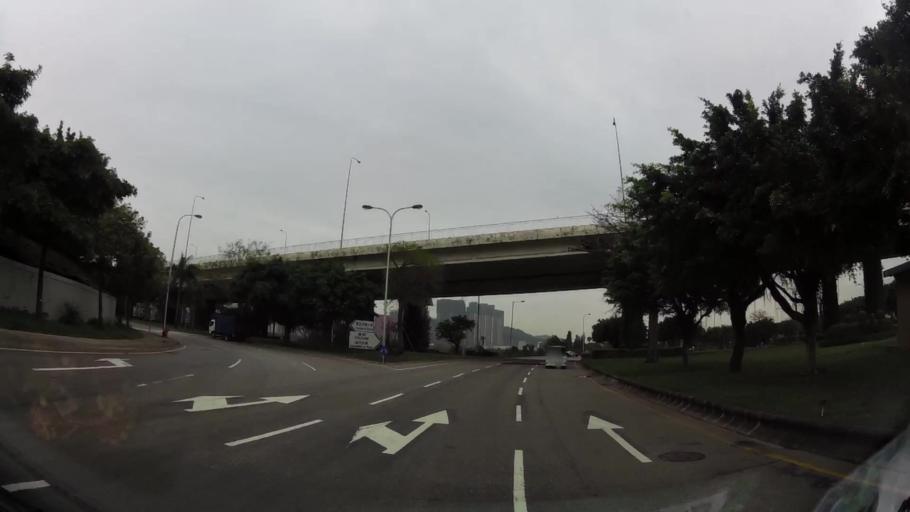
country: MO
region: Macau
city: Macau
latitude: 22.1402
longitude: 113.5529
